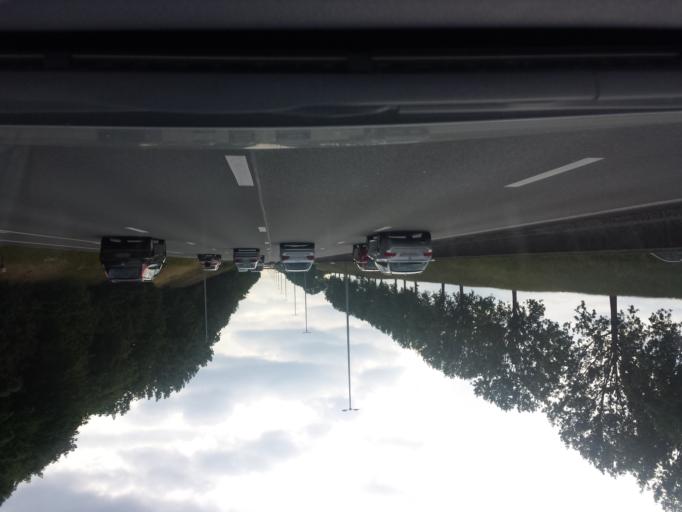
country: BE
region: Flanders
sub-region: Provincie Vlaams-Brabant
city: Bertem
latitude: 50.8621
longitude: 4.6042
